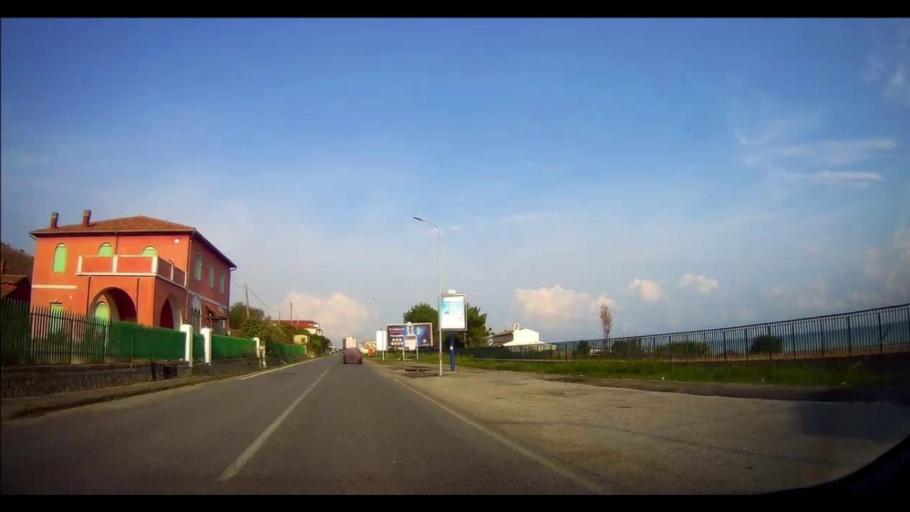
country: IT
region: Calabria
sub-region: Provincia di Cosenza
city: Cariati
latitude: 39.5096
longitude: 16.9304
